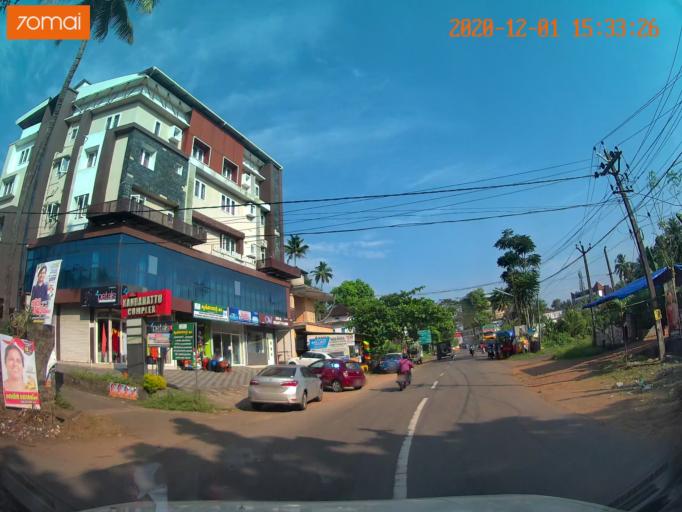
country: IN
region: Kerala
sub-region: Ernakulam
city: Muvattupuzha
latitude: 9.9766
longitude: 76.5781
